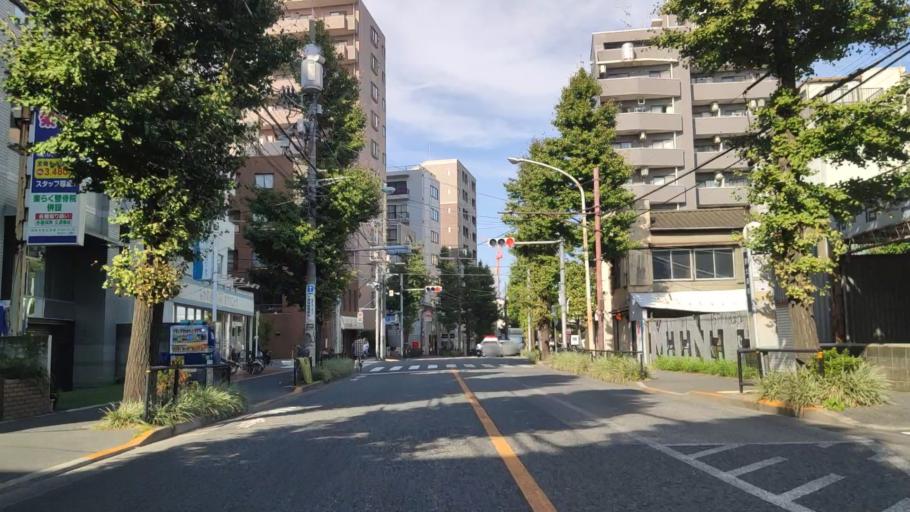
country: JP
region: Tokyo
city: Tokyo
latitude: 35.6883
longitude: 139.6689
